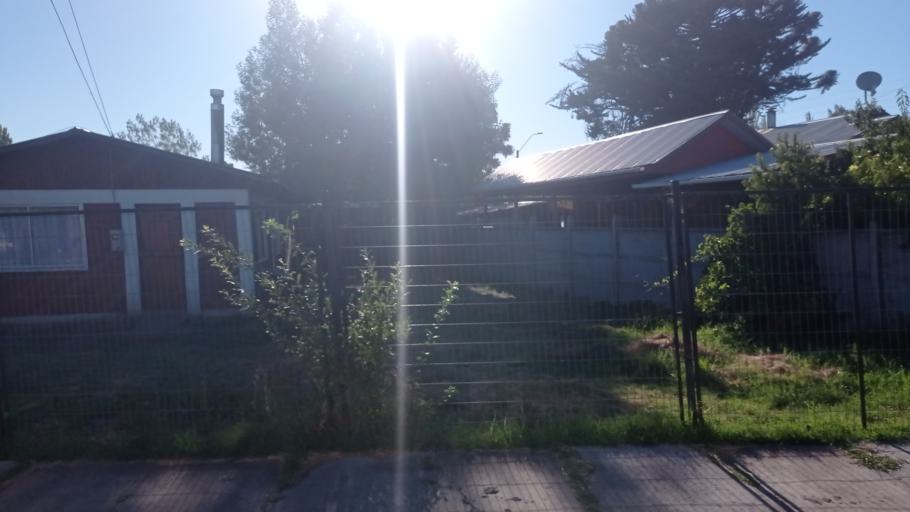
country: CL
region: Biobio
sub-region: Provincia de Biobio
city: Nacimiento
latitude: -37.5598
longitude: -72.5948
